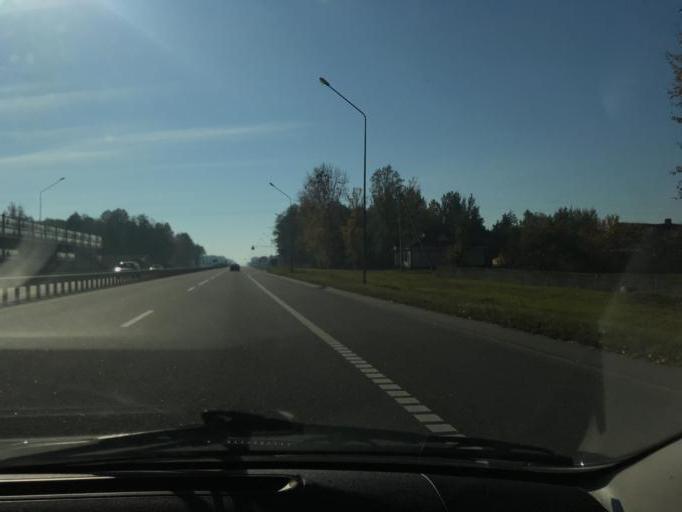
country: BY
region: Minsk
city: Slutsk
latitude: 53.2772
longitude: 27.5499
